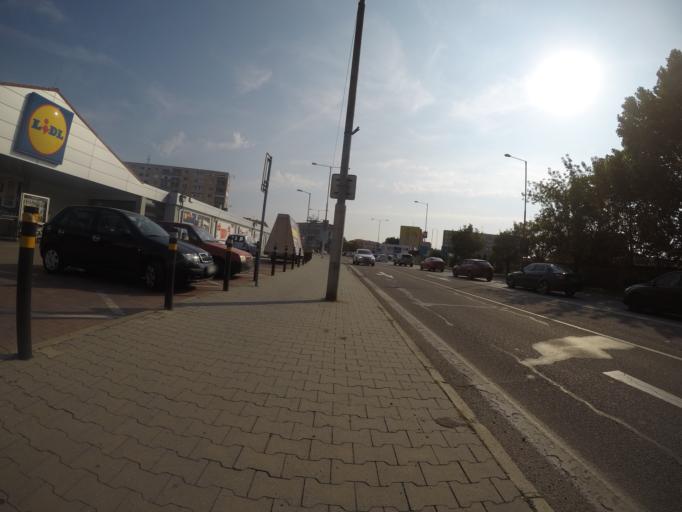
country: SK
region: Trnavsky
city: Dunajska Streda
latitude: 47.9909
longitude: 17.6184
